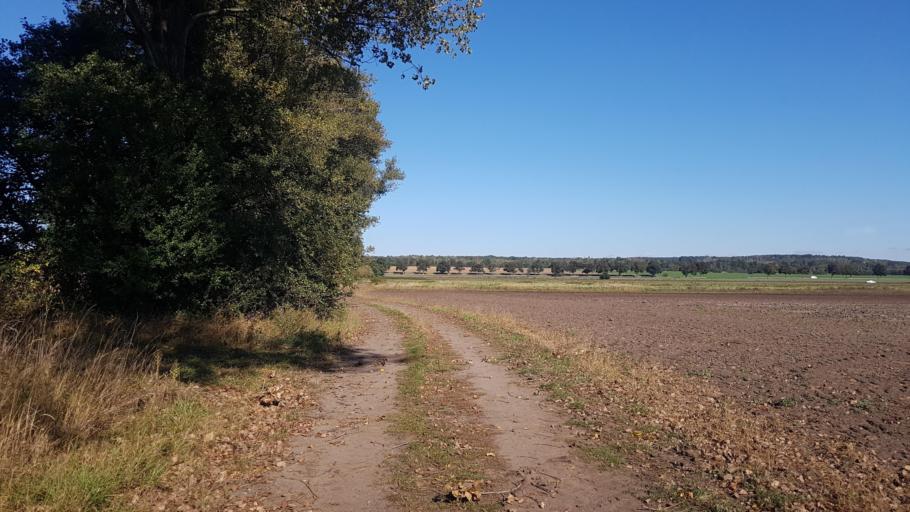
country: DE
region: Brandenburg
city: Plessa
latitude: 51.4623
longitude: 13.5871
